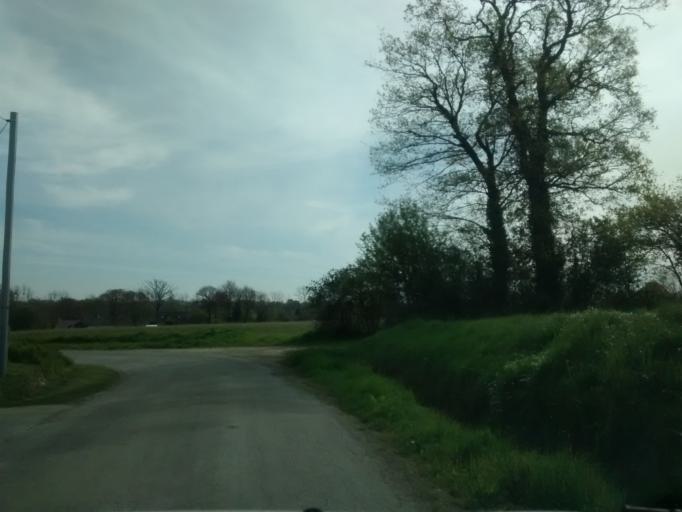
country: FR
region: Brittany
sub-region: Departement d'Ille-et-Vilaine
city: Noyal-sur-Vilaine
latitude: 48.1246
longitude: -1.5249
